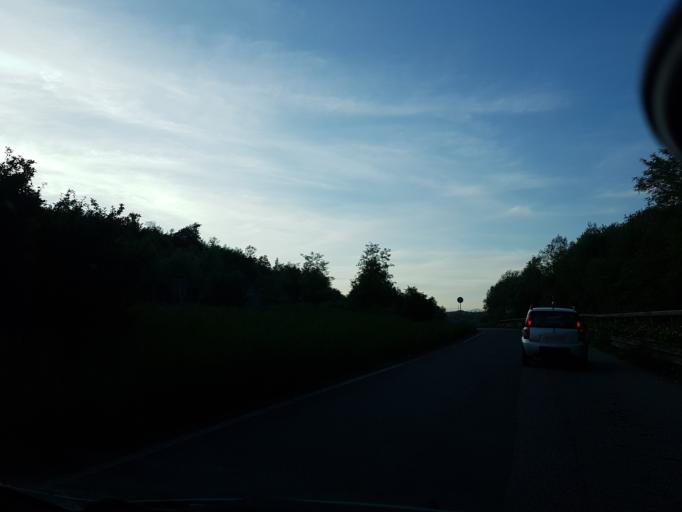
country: IT
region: Tuscany
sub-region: Provincia di Massa-Carrara
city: Aulla
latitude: 44.2152
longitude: 9.9774
